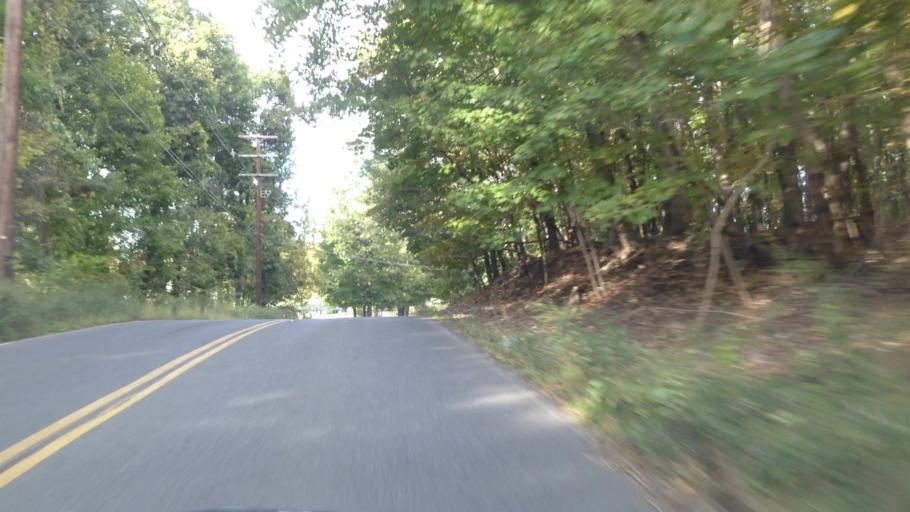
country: US
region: New York
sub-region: Ulster County
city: Kingston
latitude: 41.9191
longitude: -74.0042
